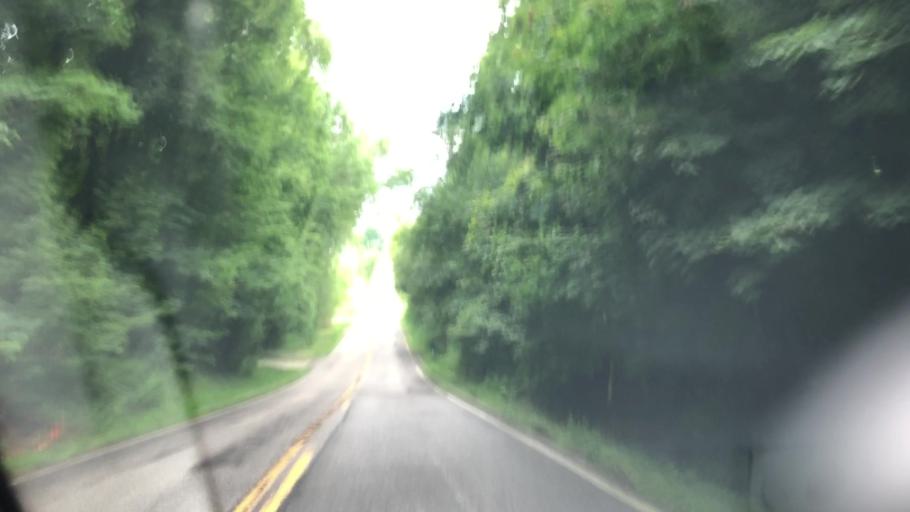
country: US
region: Ohio
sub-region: Summit County
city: Montrose-Ghent
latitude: 41.1236
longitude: -81.7159
